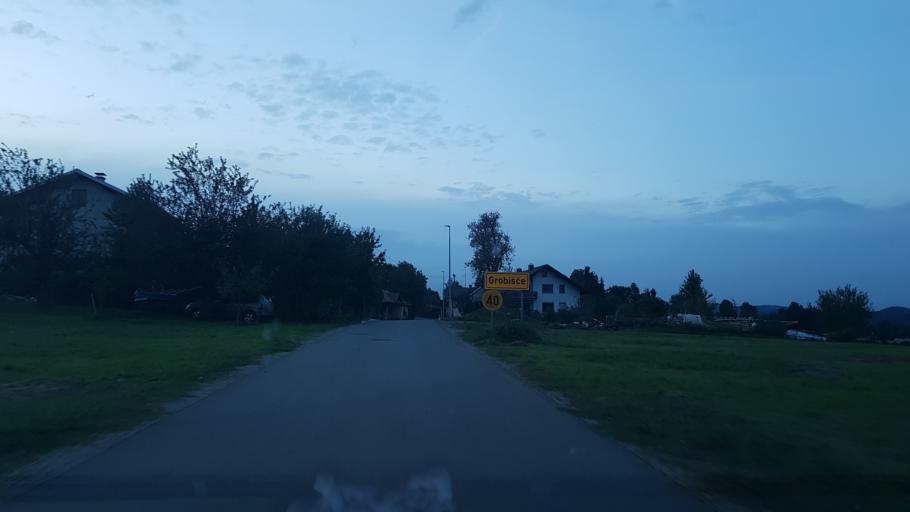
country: SI
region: Postojna
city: Postojna
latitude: 45.7481
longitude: 14.1798
